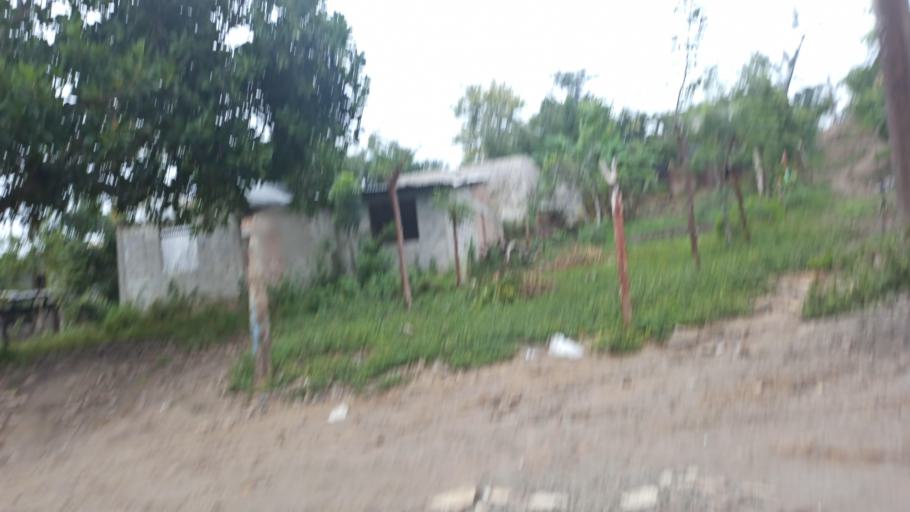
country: MX
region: Veracruz
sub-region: Papantla
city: El Chote
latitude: 20.3940
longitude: -97.3558
